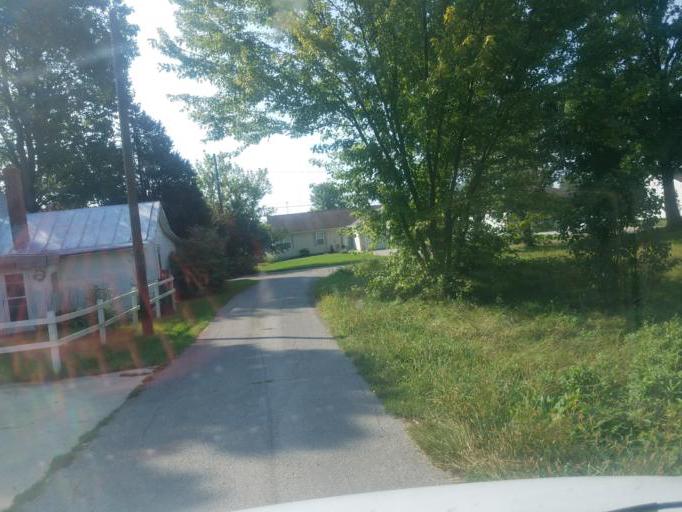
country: US
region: Ohio
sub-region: Morrow County
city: Mount Gilead
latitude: 40.5570
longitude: -82.8592
